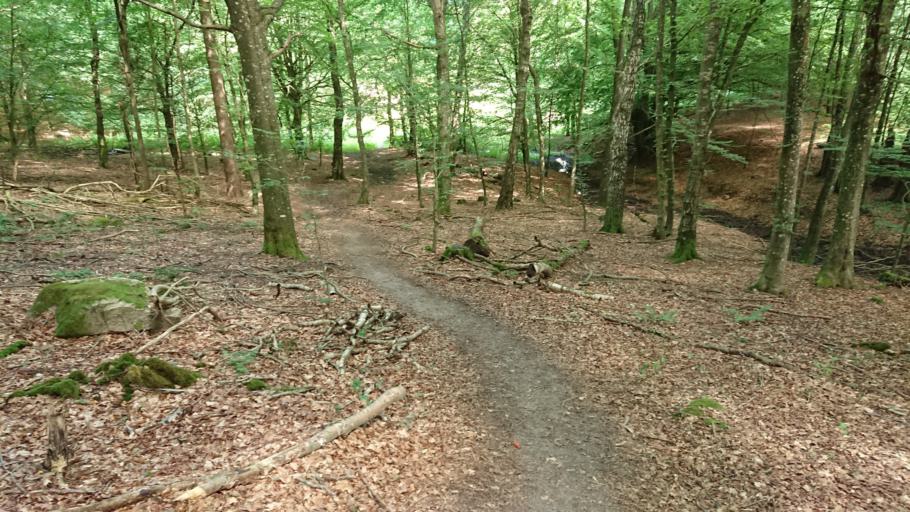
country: DK
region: North Denmark
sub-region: Hjorring Kommune
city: Sindal
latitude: 57.4490
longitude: 10.3329
